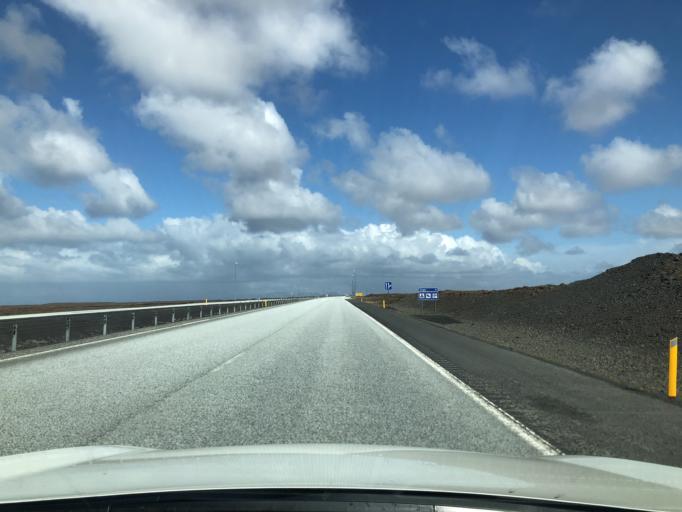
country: IS
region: Southern Peninsula
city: Vogar
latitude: 63.9710
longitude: -22.3676
